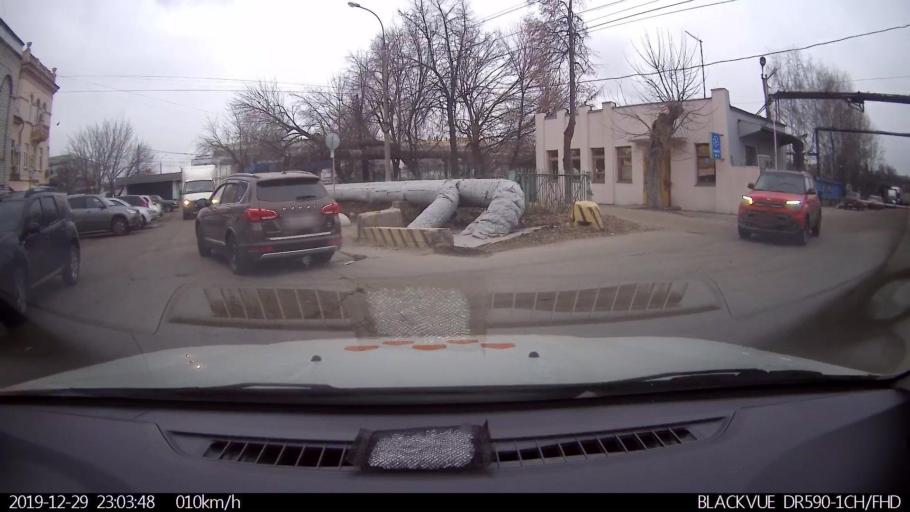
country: RU
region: Nizjnij Novgorod
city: Nizhniy Novgorod
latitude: 56.2586
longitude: 43.9020
